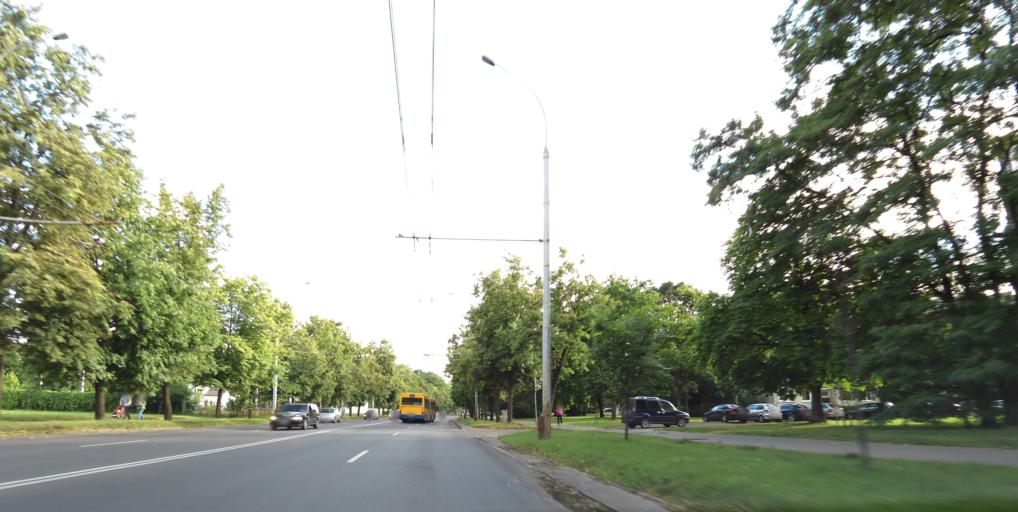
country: LT
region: Vilnius County
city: Rasos
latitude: 54.7009
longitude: 25.3032
